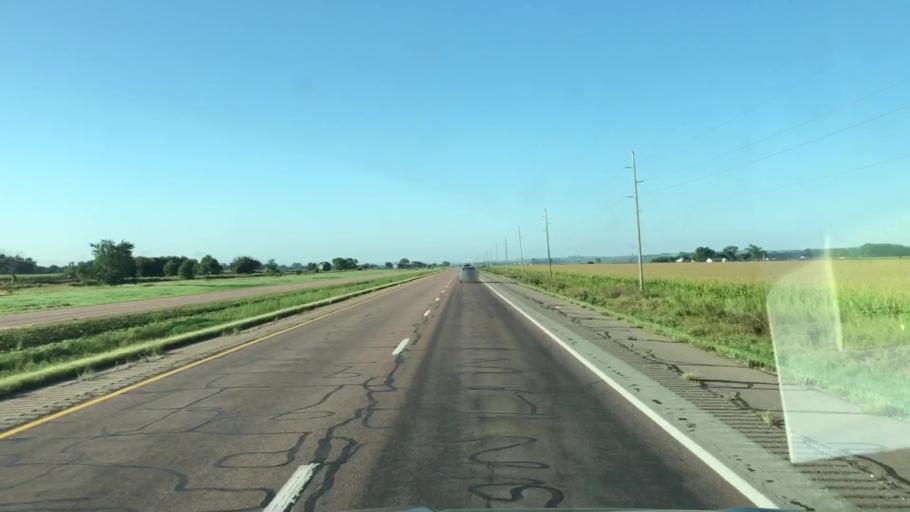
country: US
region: Iowa
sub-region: Plymouth County
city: Le Mars
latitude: 42.7094
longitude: -96.2531
